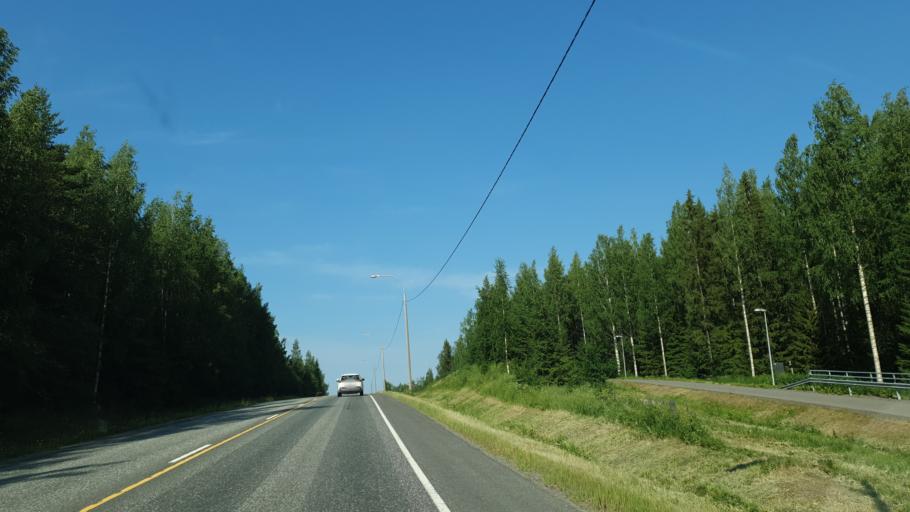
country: FI
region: Northern Savo
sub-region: Kuopio
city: Siilinjaervi
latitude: 63.1134
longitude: 27.7620
